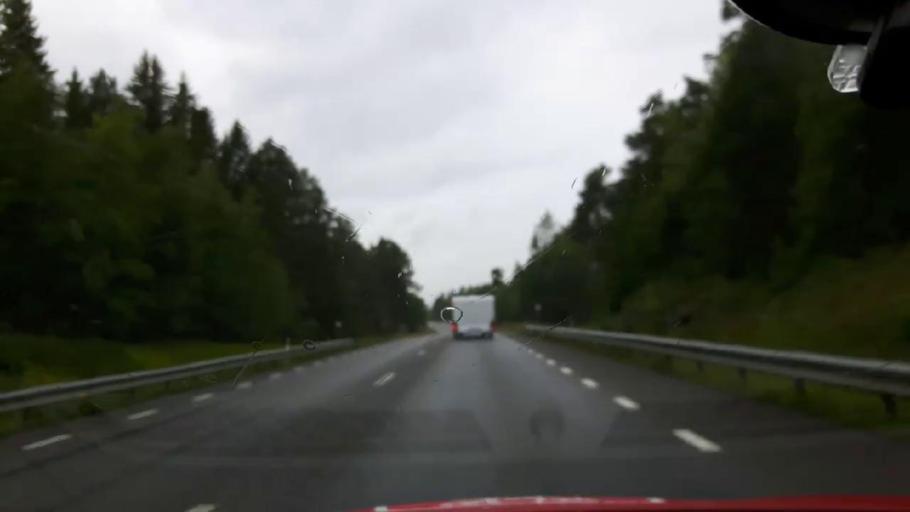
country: SE
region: Jaemtland
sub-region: Are Kommun
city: Jarpen
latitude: 63.3179
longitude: 13.5739
